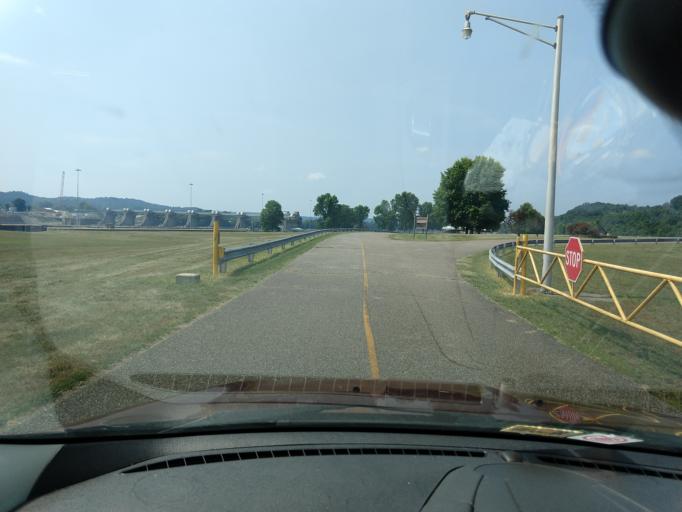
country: US
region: West Virginia
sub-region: Mason County
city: New Haven
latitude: 38.9226
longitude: -81.9104
